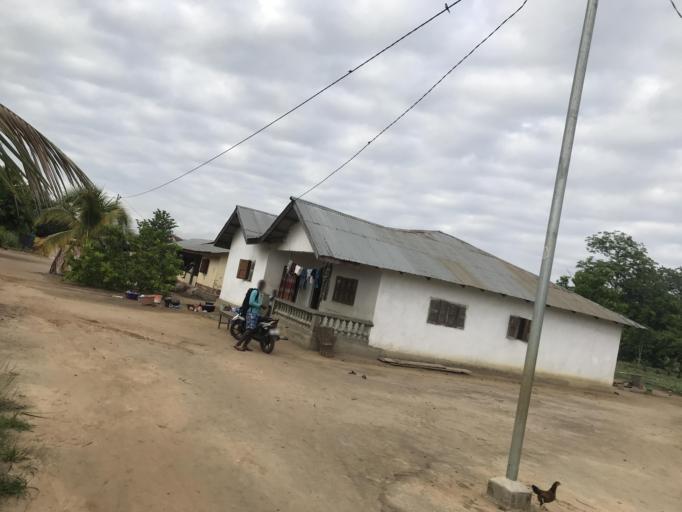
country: SL
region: Eastern Province
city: Pendembu
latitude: 8.0890
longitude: -10.6941
